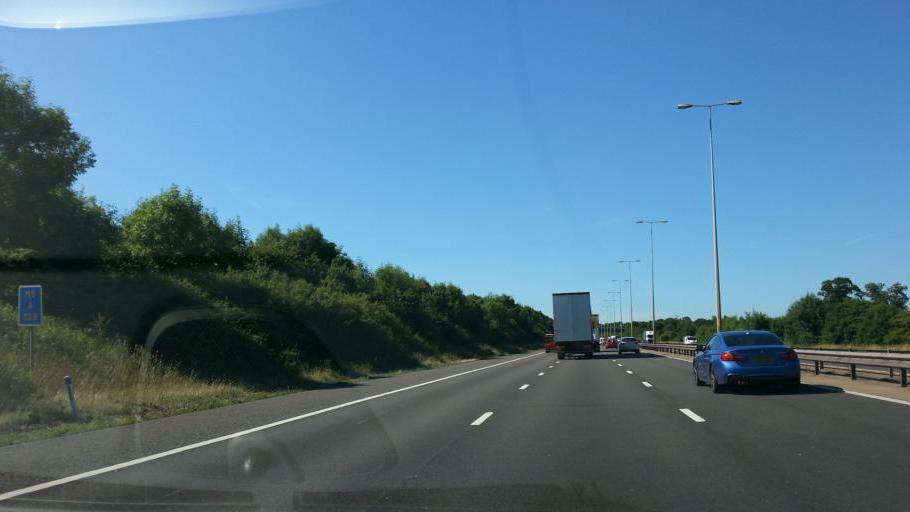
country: GB
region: England
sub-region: Worcestershire
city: Kempsey
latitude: 52.1370
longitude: -2.1976
